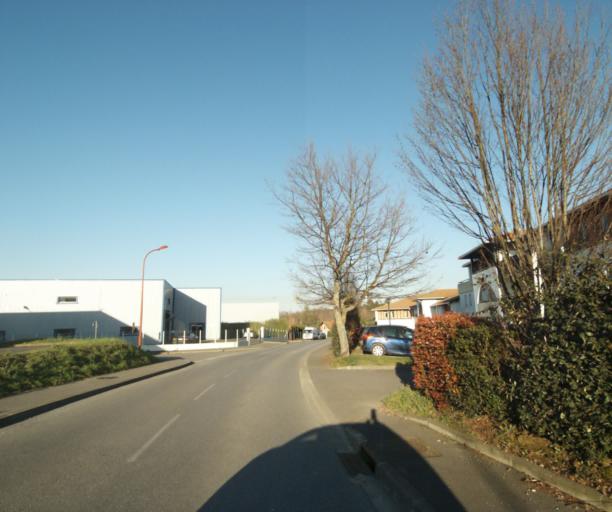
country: FR
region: Aquitaine
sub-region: Departement des Pyrenees-Atlantiques
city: Urrugne
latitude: 43.3455
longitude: -1.6921
